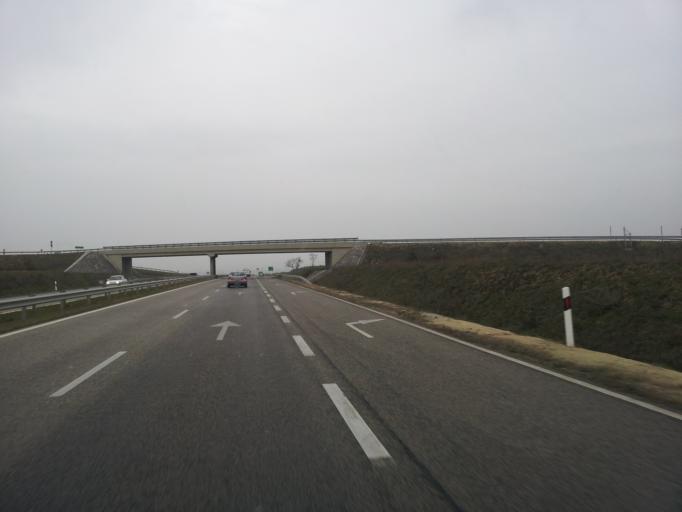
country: HU
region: Veszprem
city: Herend
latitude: 47.1185
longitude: 17.8043
